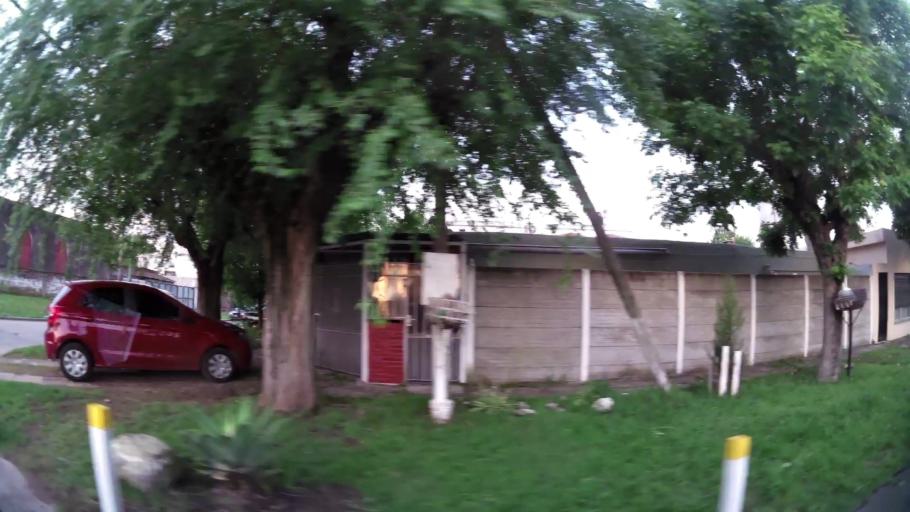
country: AR
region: Buenos Aires
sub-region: Partido de Lomas de Zamora
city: Lomas de Zamora
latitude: -34.7609
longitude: -58.3690
